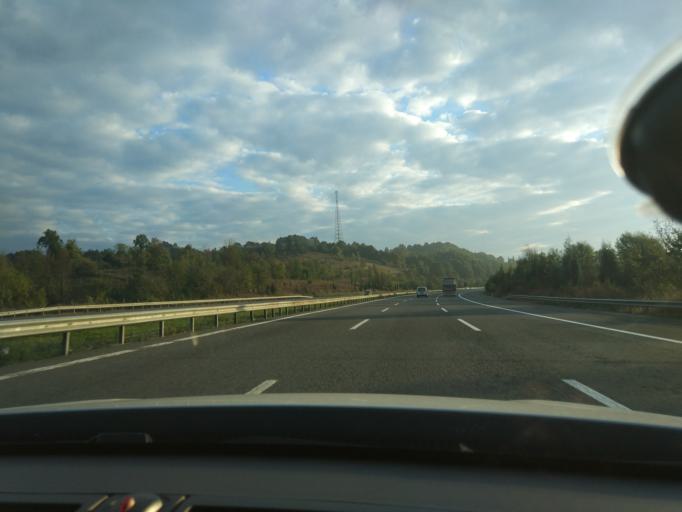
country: TR
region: Sakarya
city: Hendek
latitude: 40.7678
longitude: 30.7624
